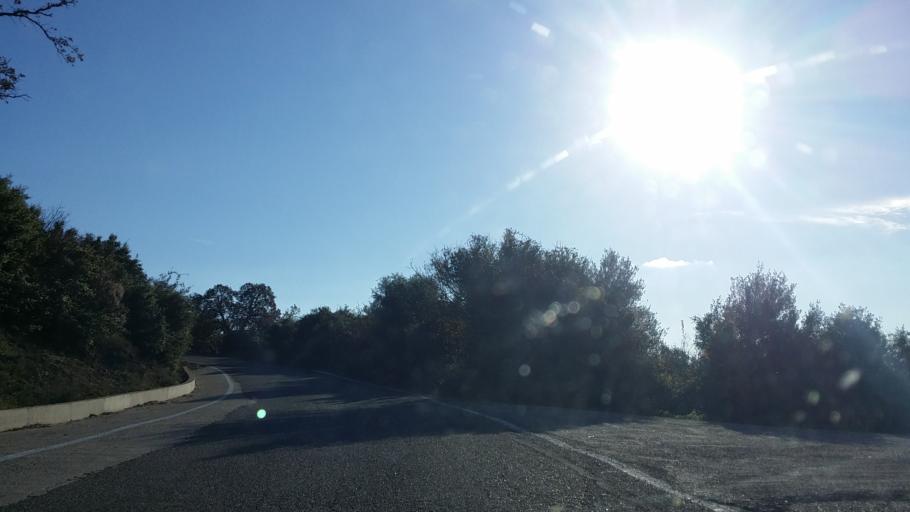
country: GR
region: West Greece
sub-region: Nomos Aitolias kai Akarnanias
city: Fitiai
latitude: 38.6399
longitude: 21.1877
